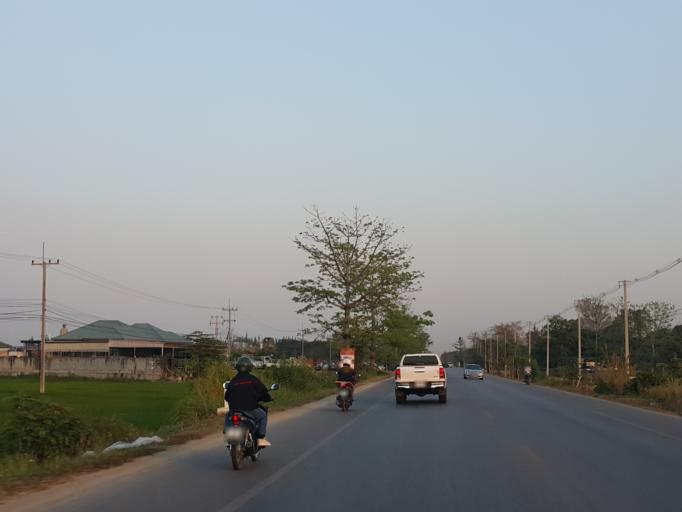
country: TH
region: Chiang Mai
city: San Sai
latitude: 18.8559
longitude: 99.0004
